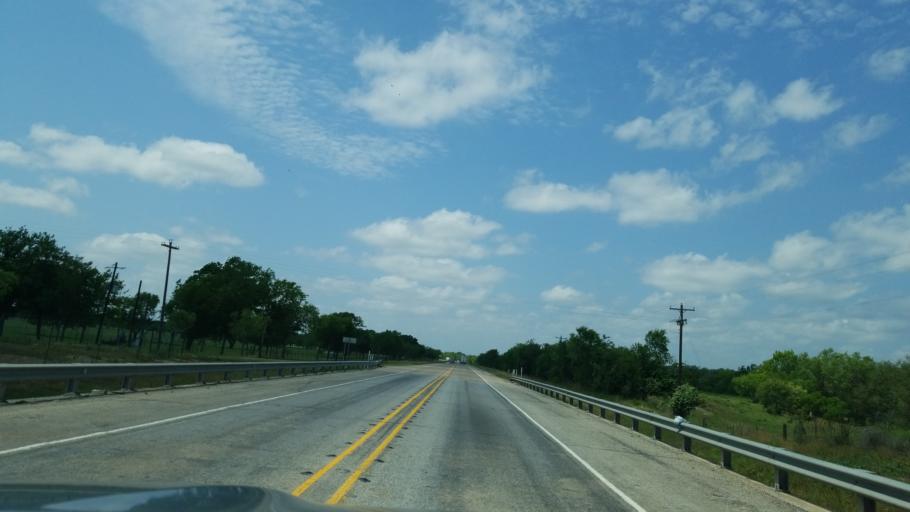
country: US
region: Texas
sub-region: Frio County
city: Pearsall
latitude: 28.9928
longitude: -99.2271
